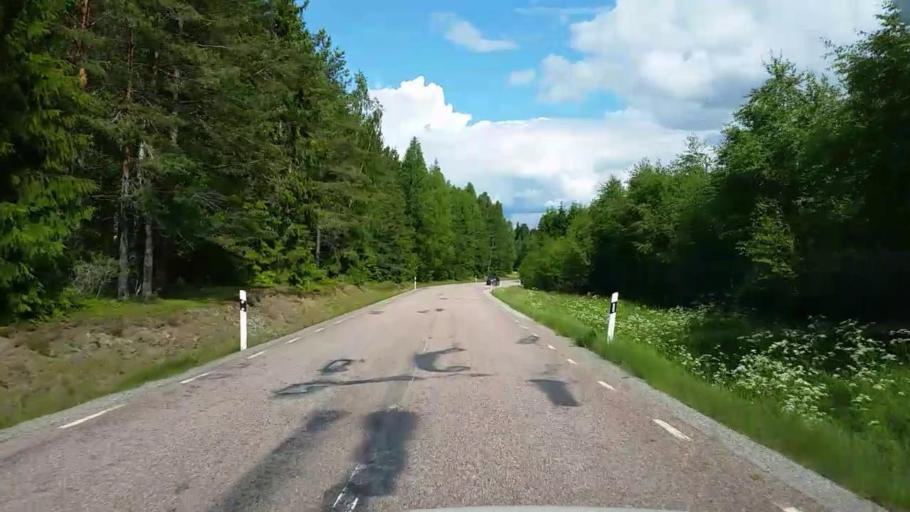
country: SE
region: Vaestmanland
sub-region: Fagersta Kommun
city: Fagersta
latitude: 59.9243
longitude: 15.8300
